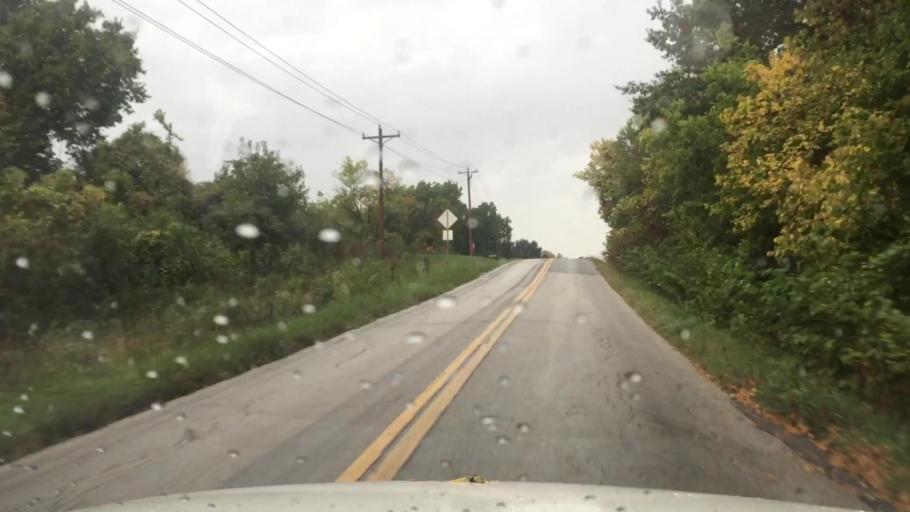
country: US
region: Missouri
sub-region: Boone County
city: Columbia
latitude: 38.9327
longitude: -92.4913
